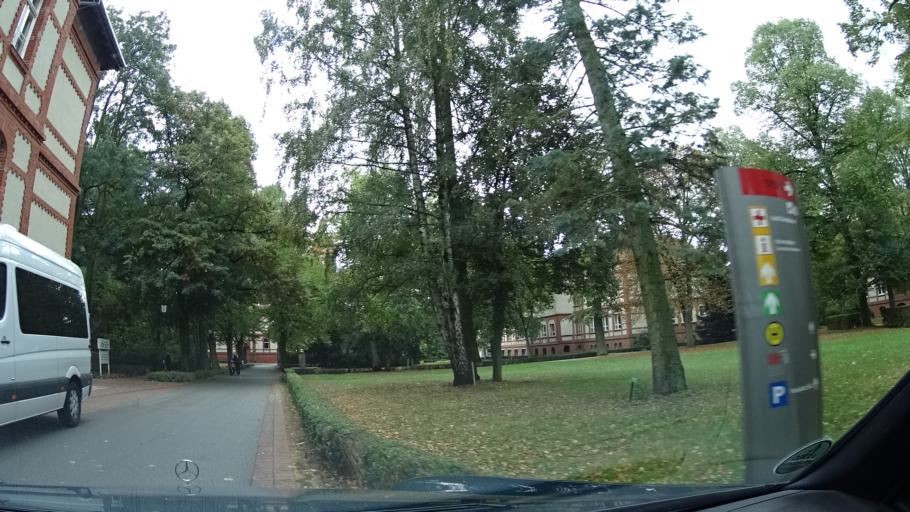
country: DE
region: Brandenburg
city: Neuruppin
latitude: 52.9079
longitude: 12.7985
